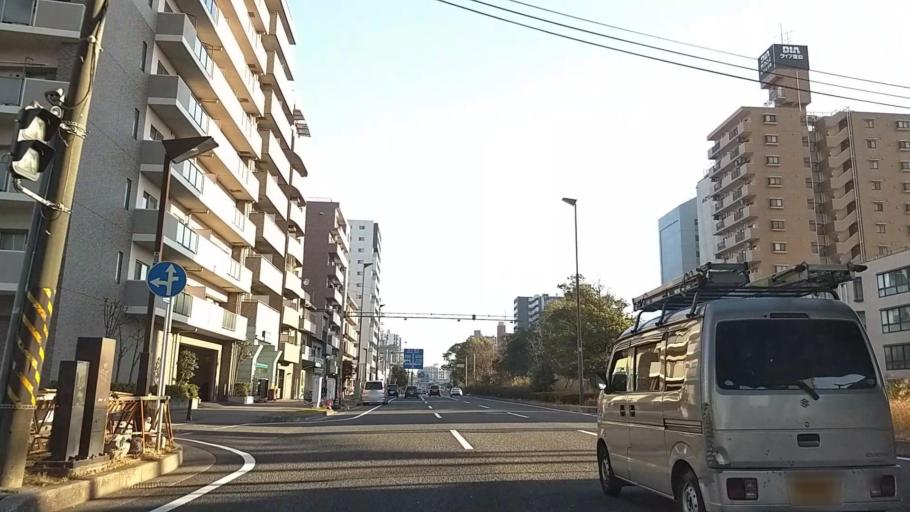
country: JP
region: Kanagawa
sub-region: Kawasaki-shi
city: Kawasaki
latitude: 35.5220
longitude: 139.6935
